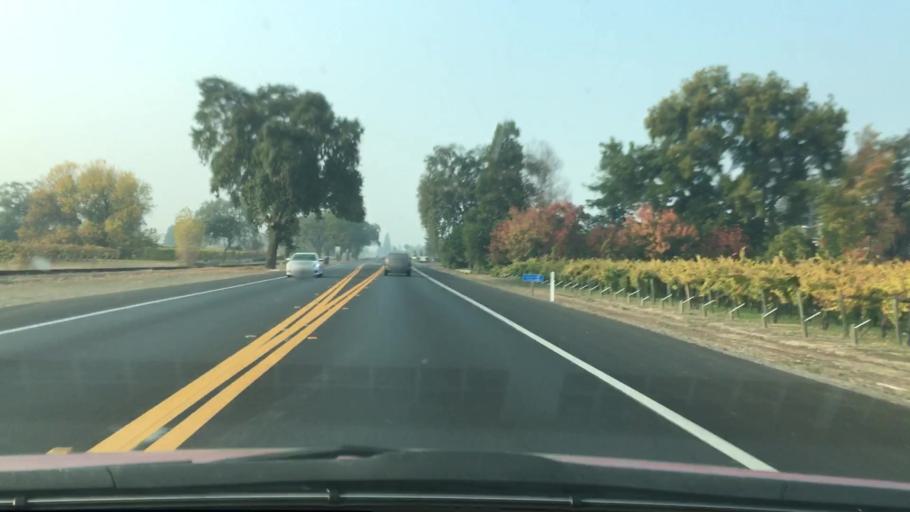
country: US
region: California
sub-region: Napa County
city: Yountville
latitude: 38.4466
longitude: -122.4115
